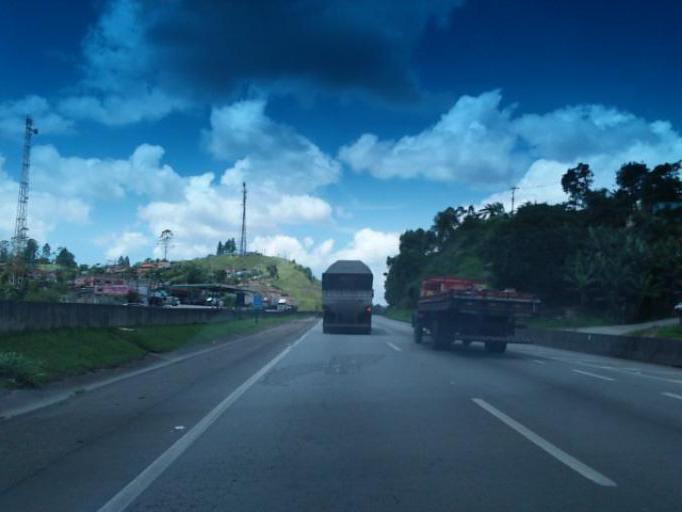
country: BR
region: Sao Paulo
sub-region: Juquitiba
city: Juquitiba
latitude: -23.9823
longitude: -47.1461
